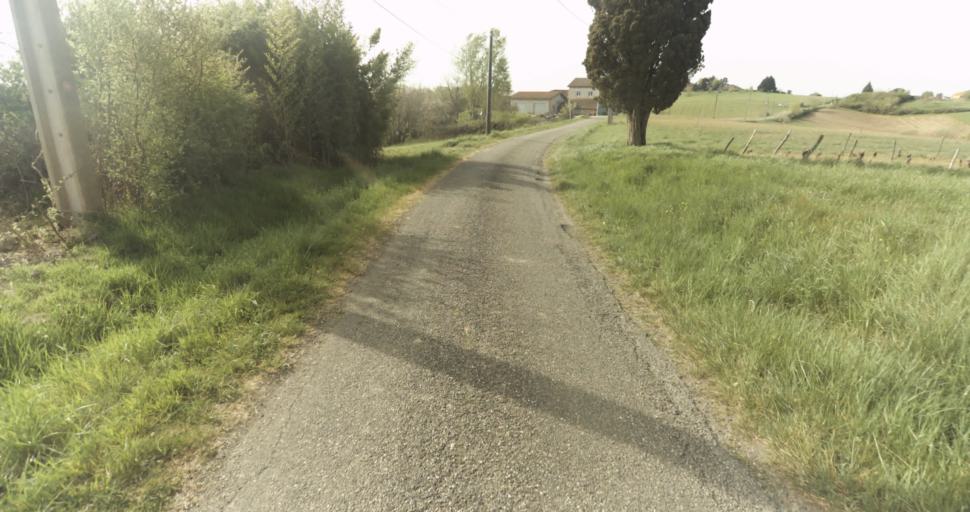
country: FR
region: Midi-Pyrenees
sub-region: Departement du Tarn-et-Garonne
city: Moissac
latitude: 44.1523
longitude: 1.0444
